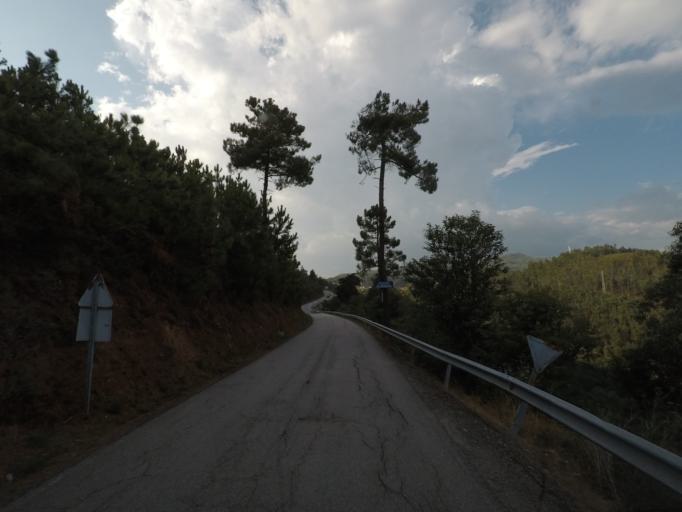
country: PT
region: Porto
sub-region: Baiao
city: Valadares
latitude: 41.1813
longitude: -7.9365
